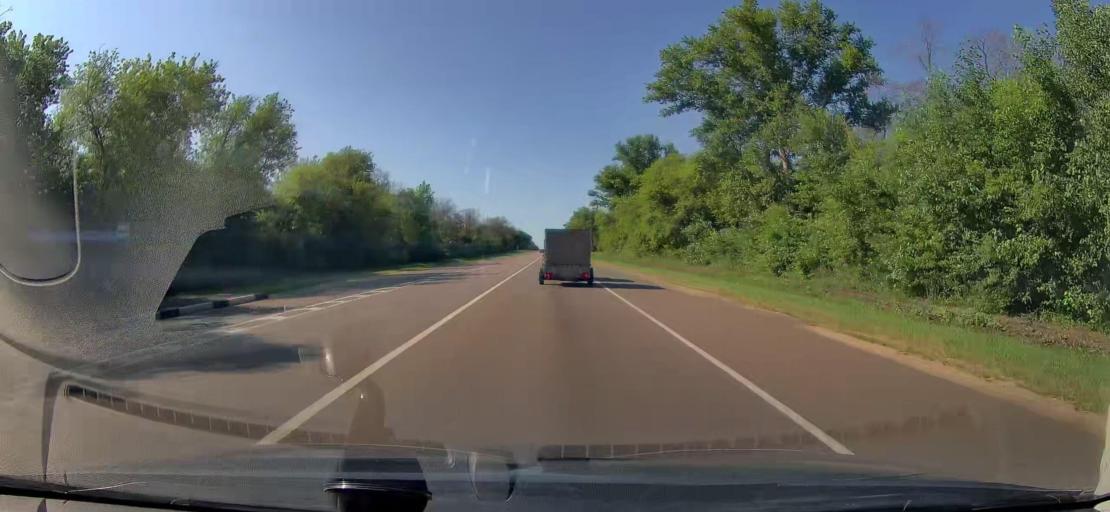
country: RU
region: Orjol
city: Kromy
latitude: 52.6075
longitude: 35.7620
